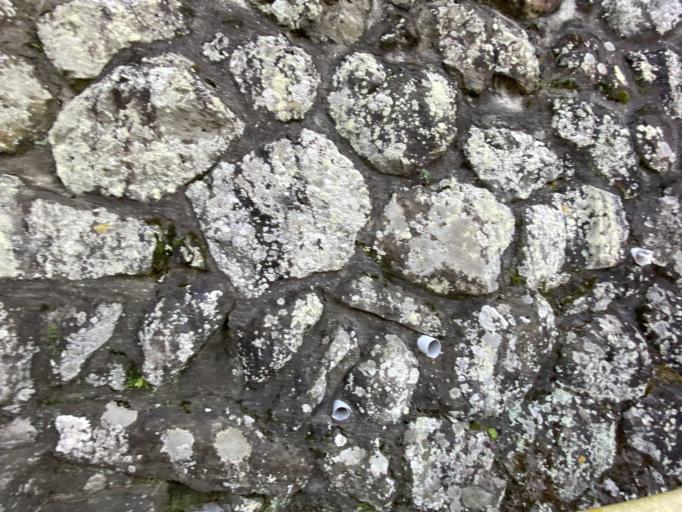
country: JP
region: Nagasaki
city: Nagasaki-shi
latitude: 32.7482
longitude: 129.8867
